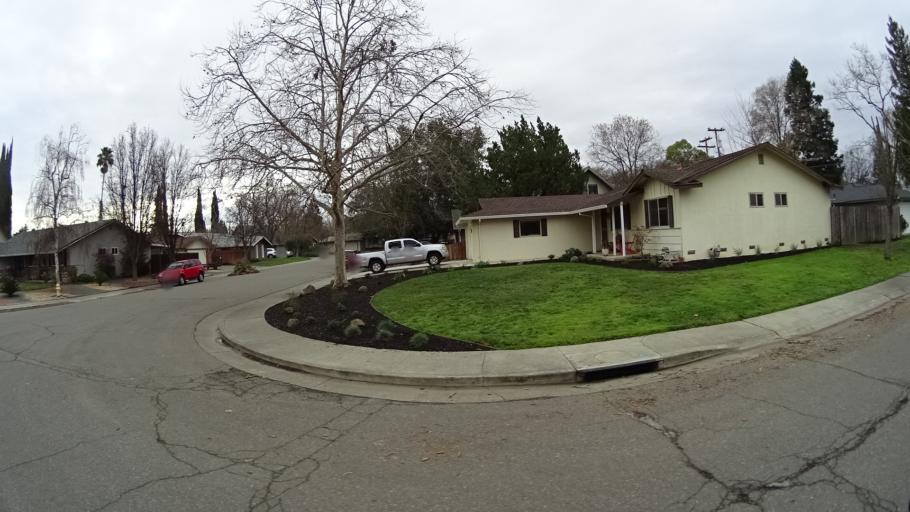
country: US
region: California
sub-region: Yolo County
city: Davis
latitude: 38.5615
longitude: -121.7218
